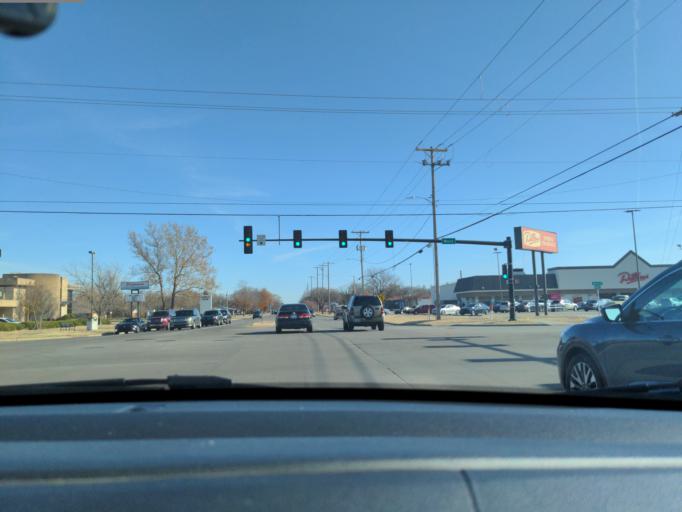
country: US
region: Kansas
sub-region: Sedgwick County
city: Wichita
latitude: 37.6947
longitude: -97.3900
